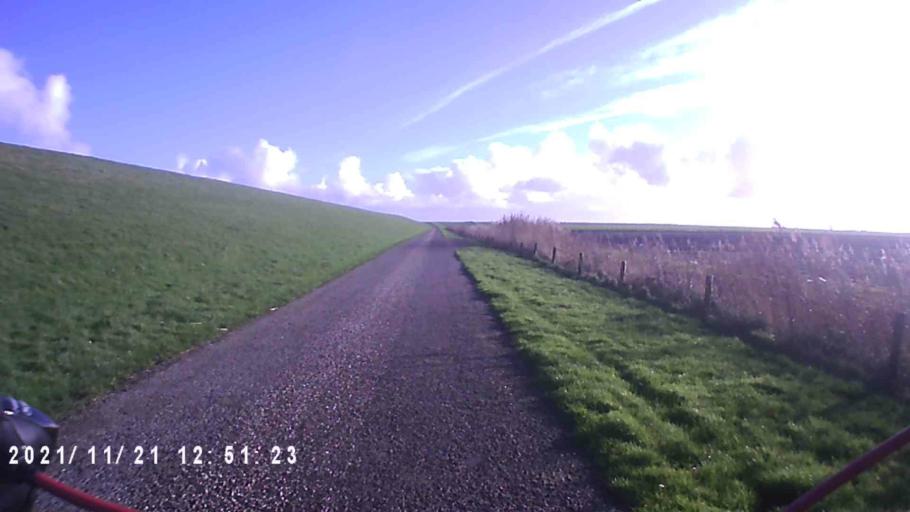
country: NL
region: Friesland
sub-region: Gemeente Dongeradeel
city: Anjum
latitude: 53.4010
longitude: 6.1246
